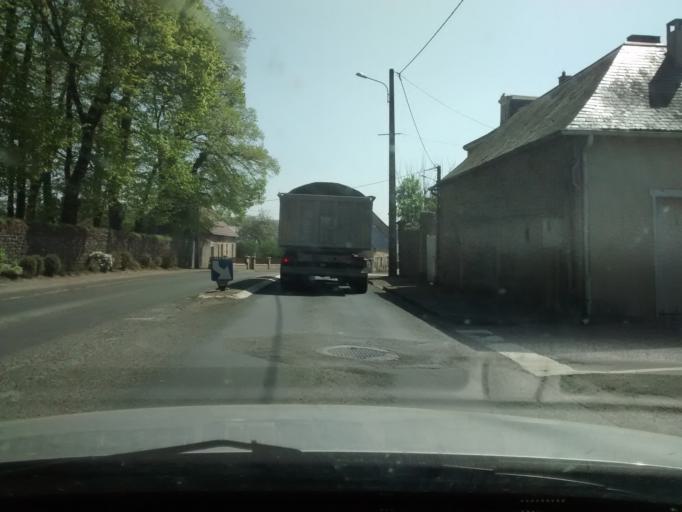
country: FR
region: Pays de la Loire
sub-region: Departement de la Sarthe
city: Loue
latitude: 48.0210
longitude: -0.1171
